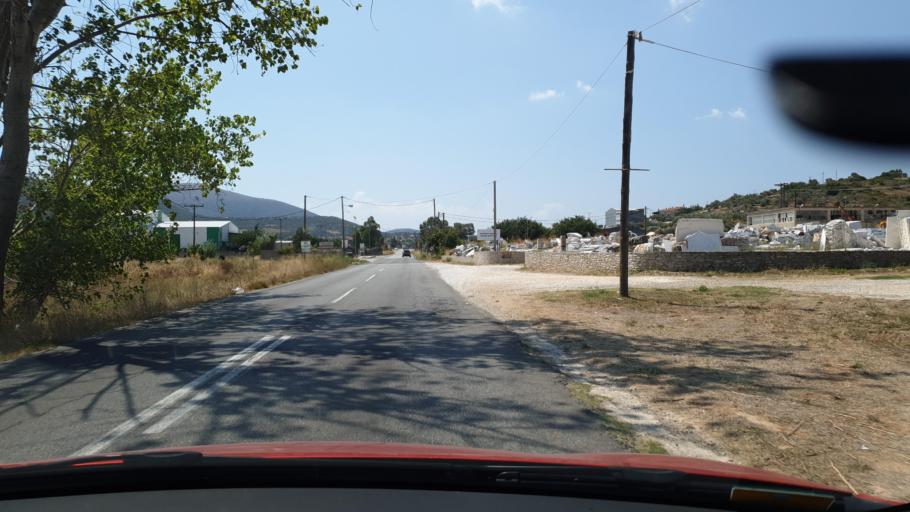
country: GR
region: Central Greece
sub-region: Nomos Evvoias
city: Aliveri
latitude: 38.3975
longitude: 24.1024
